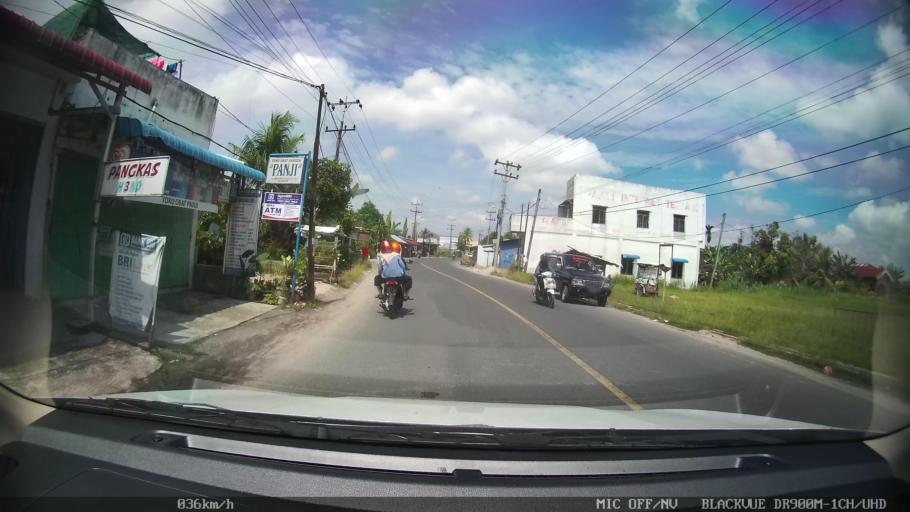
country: ID
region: North Sumatra
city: Percut
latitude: 3.6074
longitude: 98.7867
